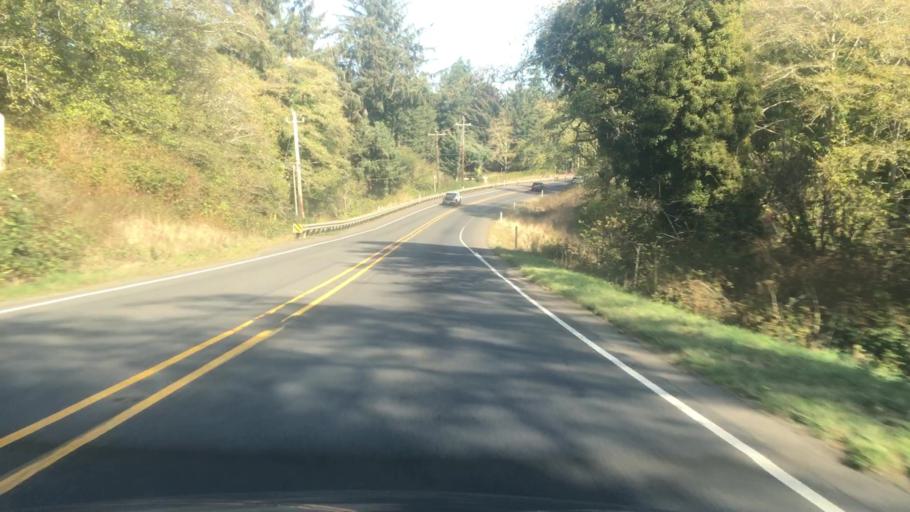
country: US
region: Oregon
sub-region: Lincoln County
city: Lincoln City
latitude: 45.0038
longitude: -123.9846
